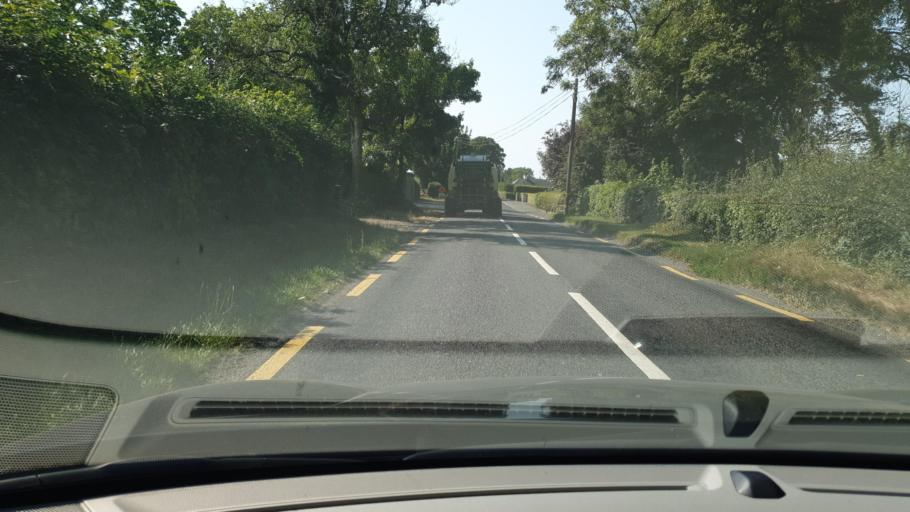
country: IE
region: Leinster
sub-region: An Mhi
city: Trim
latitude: 53.5823
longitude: -6.8495
